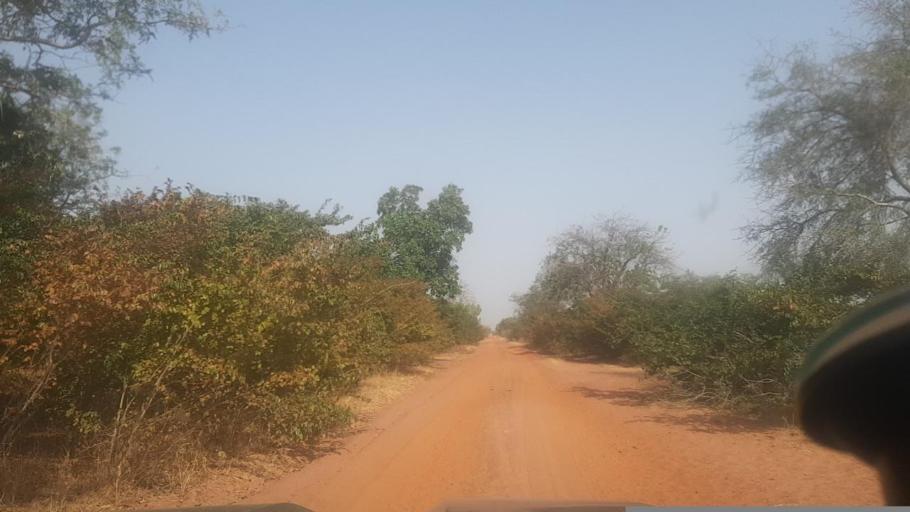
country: ML
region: Segou
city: Bla
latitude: 12.8535
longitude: -5.9801
